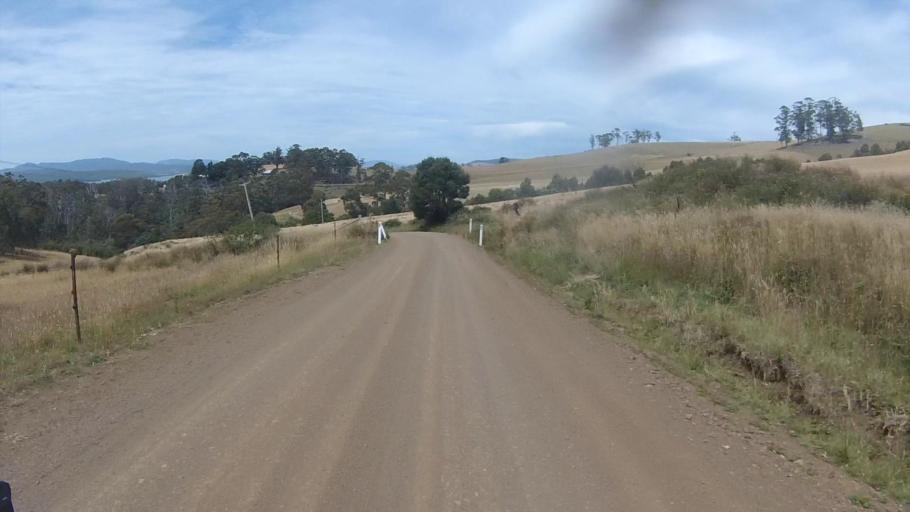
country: AU
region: Tasmania
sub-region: Sorell
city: Sorell
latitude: -42.7842
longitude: 147.8428
